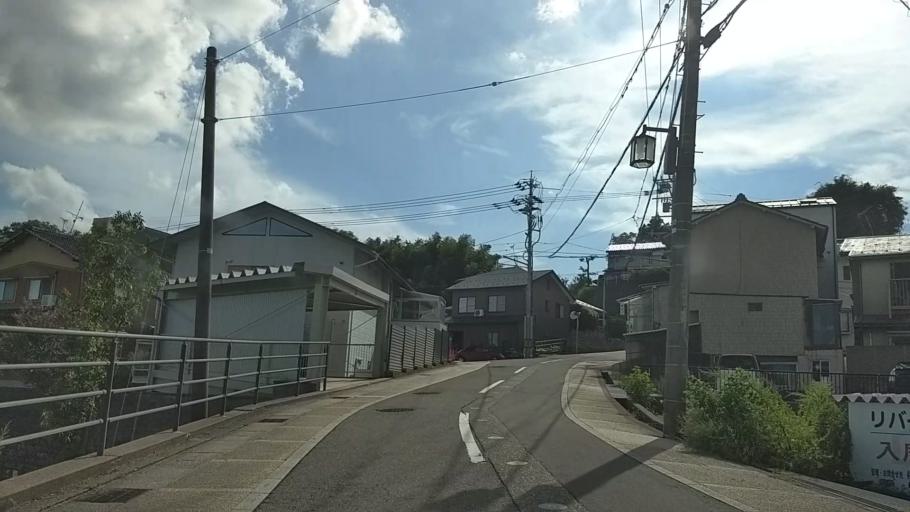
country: JP
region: Ishikawa
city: Nonoichi
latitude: 36.5471
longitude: 136.6615
